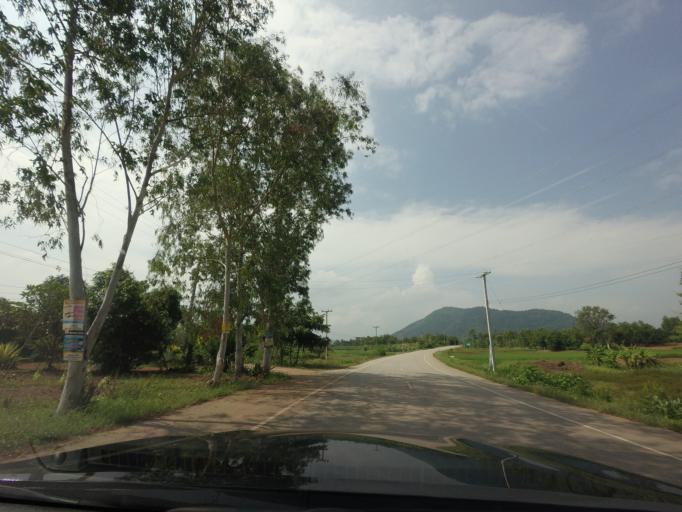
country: LA
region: Xiagnabouli
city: Muang Kenthao
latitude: 17.6819
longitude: 101.4087
